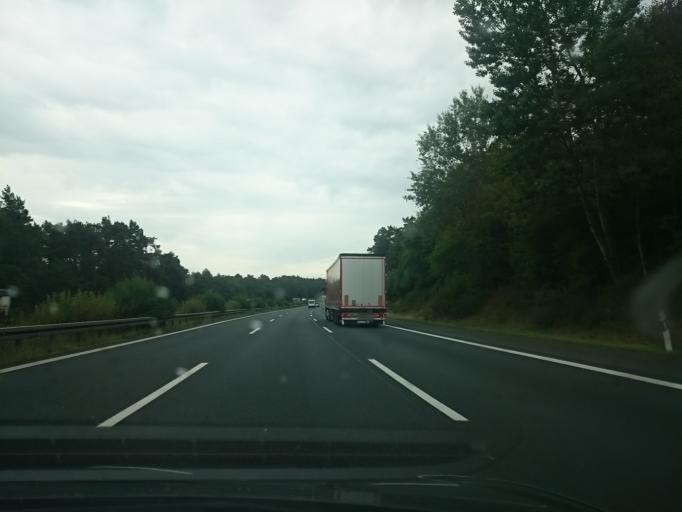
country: DE
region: Brandenburg
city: Beelitz
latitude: 52.2347
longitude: 12.9170
